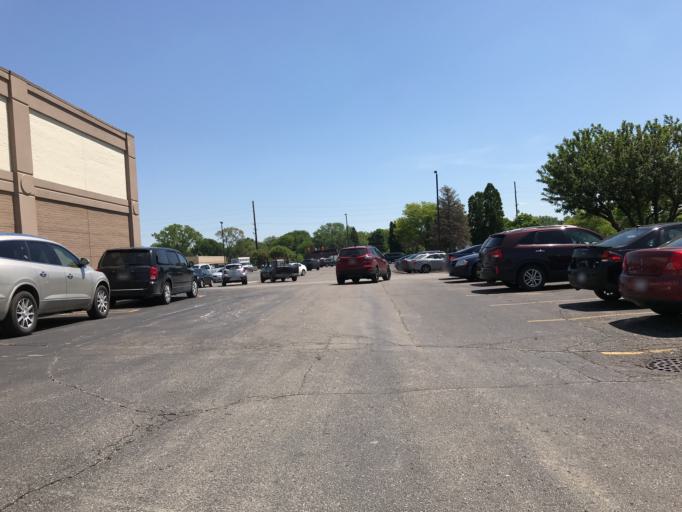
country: US
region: Michigan
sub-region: Oakland County
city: West Bloomfield Township
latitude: 42.5394
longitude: -83.3627
